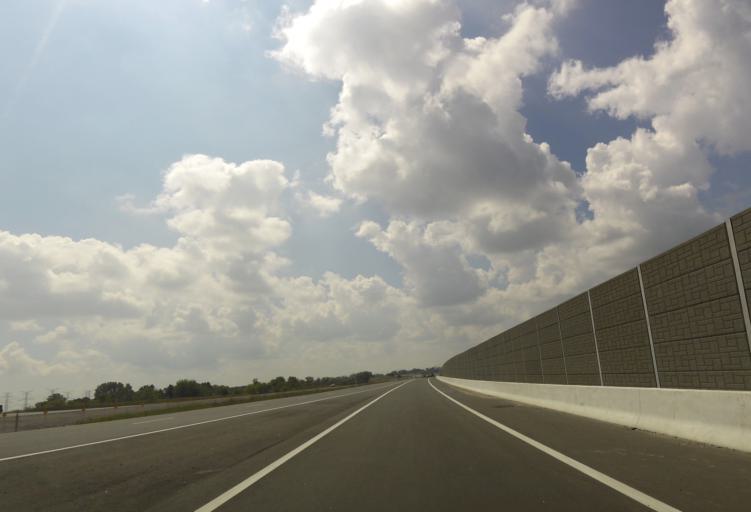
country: CA
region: Ontario
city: Oshawa
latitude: 43.9498
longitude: -78.9460
